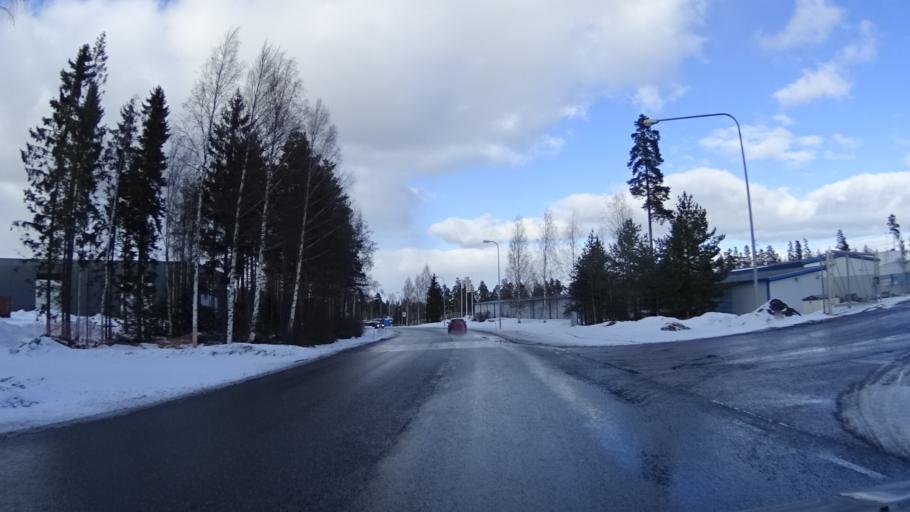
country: FI
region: Uusimaa
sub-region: Helsinki
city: Vantaa
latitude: 60.3051
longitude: 25.0938
